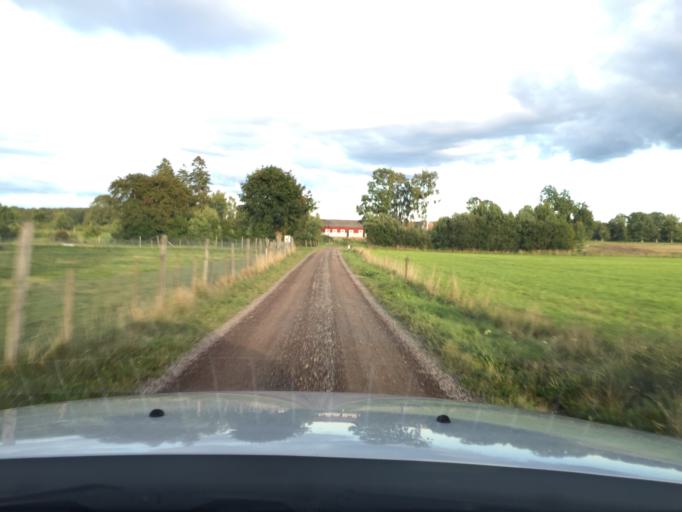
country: SE
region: Skane
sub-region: Hassleholms Kommun
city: Sosdala
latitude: 56.0293
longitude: 13.7275
